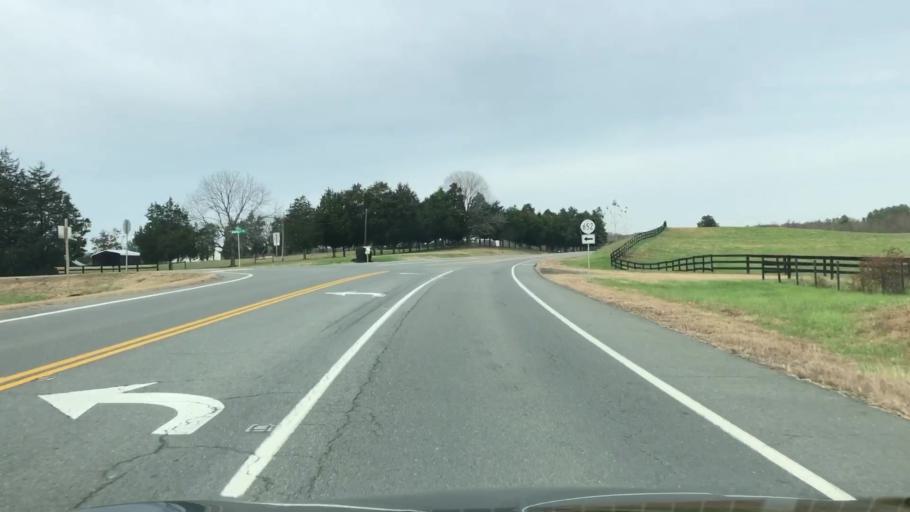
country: US
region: Virginia
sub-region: Fauquier County
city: New Baltimore
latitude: 38.7559
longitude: -77.6750
